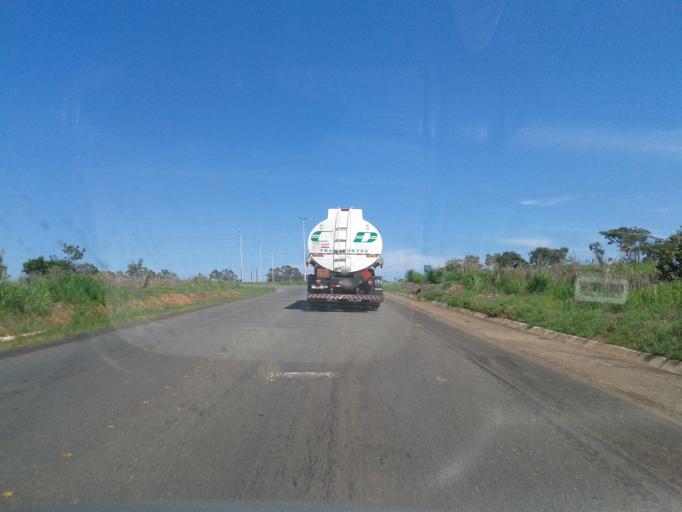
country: BR
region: Goias
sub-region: Bela Vista De Goias
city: Bela Vista de Goias
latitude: -17.0361
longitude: -48.9480
